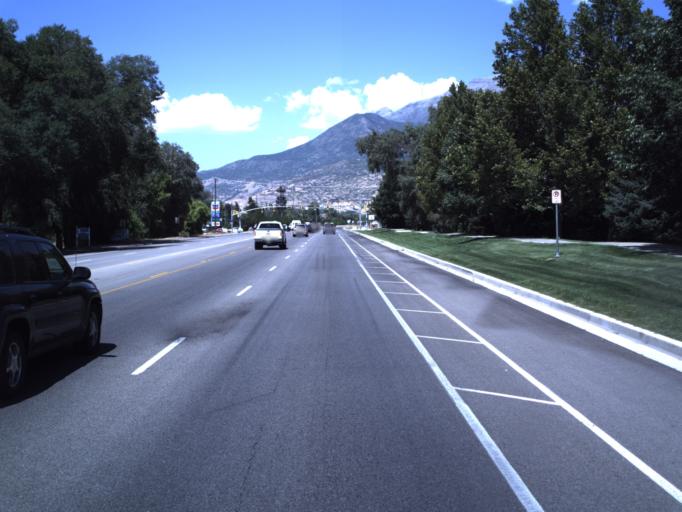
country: US
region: Utah
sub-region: Utah County
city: Orem
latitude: 40.2805
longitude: -111.6581
